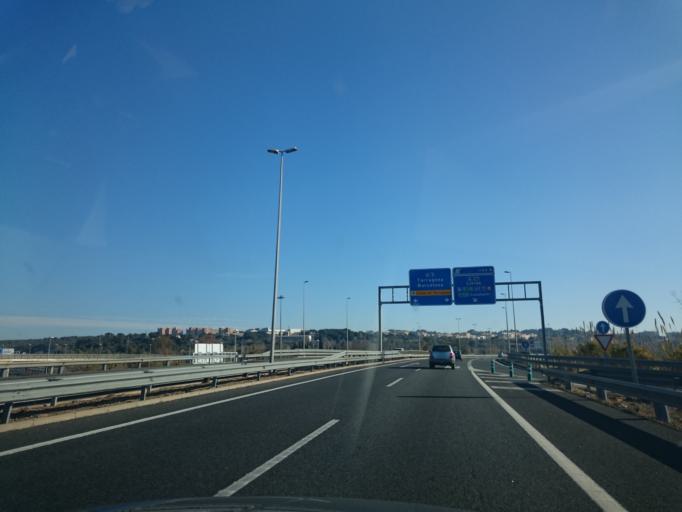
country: ES
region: Catalonia
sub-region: Provincia de Tarragona
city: Tarragona
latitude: 41.1291
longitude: 1.2273
